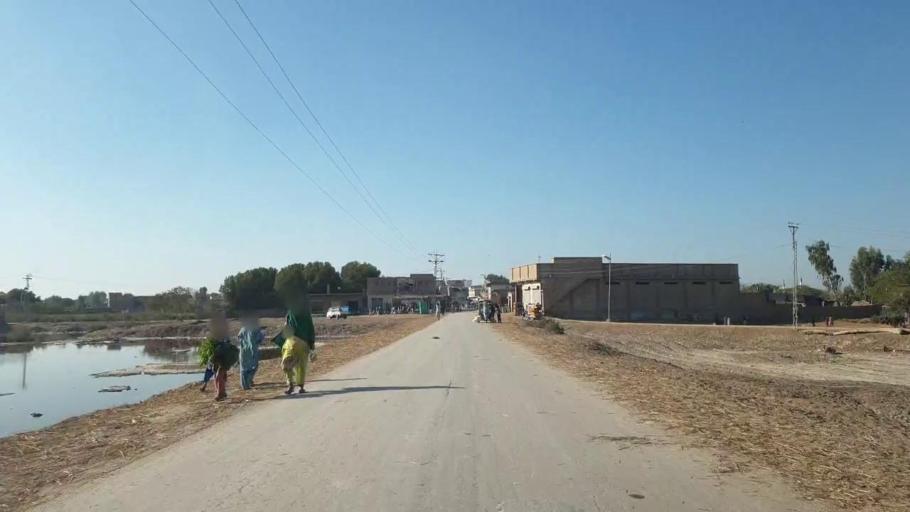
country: PK
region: Sindh
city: New Badah
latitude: 27.3267
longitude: 68.0294
